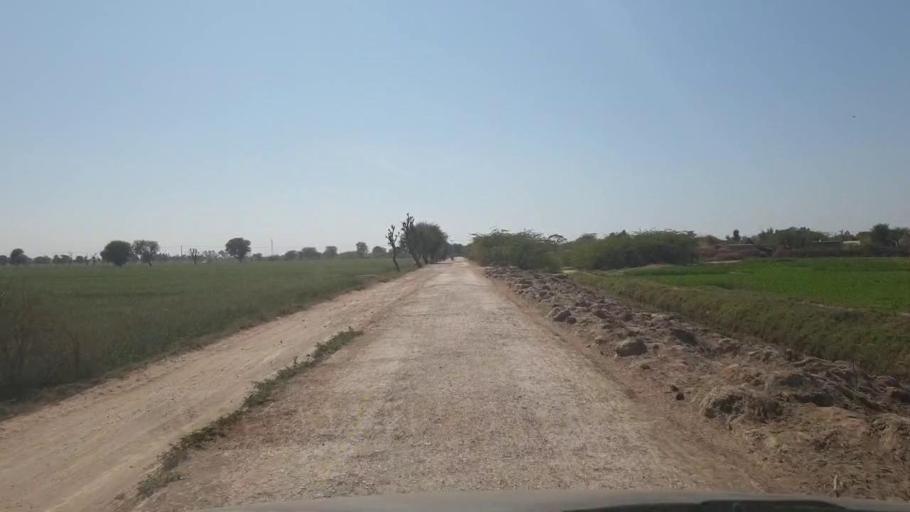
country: PK
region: Sindh
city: Dhoro Naro
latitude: 25.4728
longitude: 69.6080
